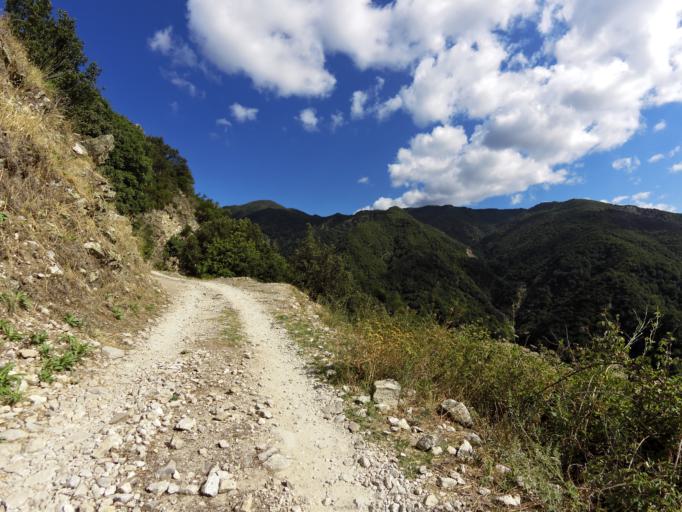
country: IT
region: Calabria
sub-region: Provincia di Reggio Calabria
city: Bivongi
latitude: 38.4910
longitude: 16.4061
